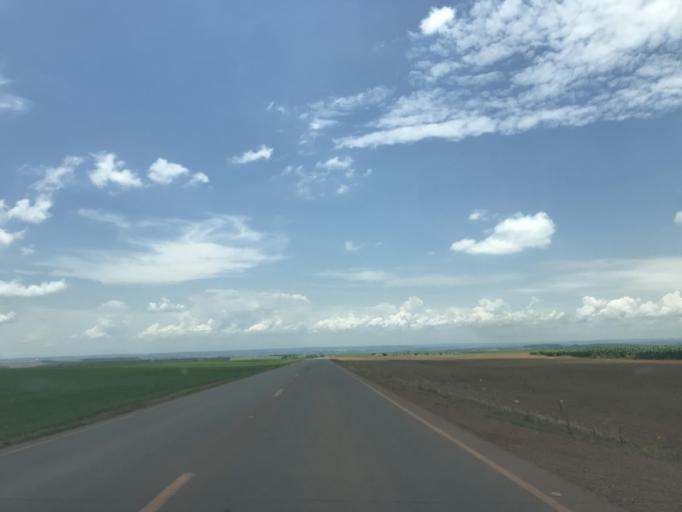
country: BR
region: Goias
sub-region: Vianopolis
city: Vianopolis
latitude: -16.5505
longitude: -48.2706
